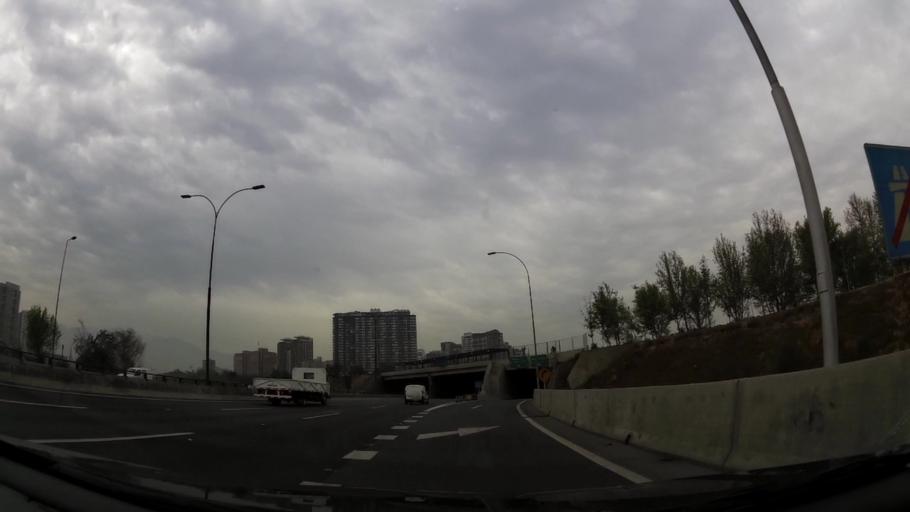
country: CL
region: Santiago Metropolitan
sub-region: Provincia de Santiago
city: Santiago
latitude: -33.4297
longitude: -70.6623
